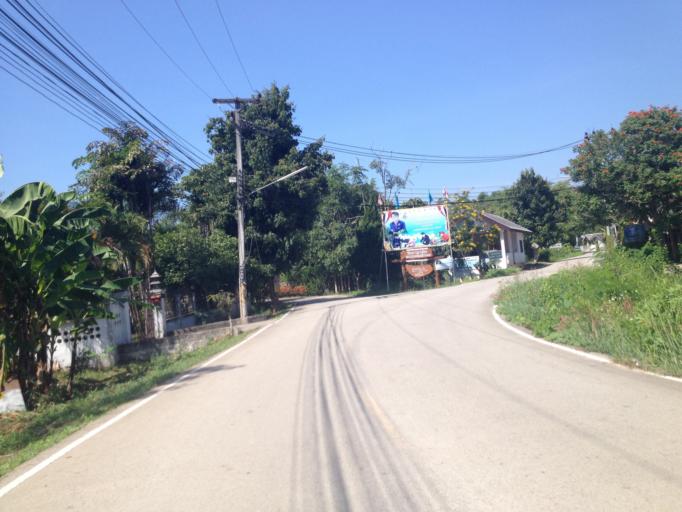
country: TH
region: Chiang Mai
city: Hang Dong
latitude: 18.7143
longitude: 98.9101
